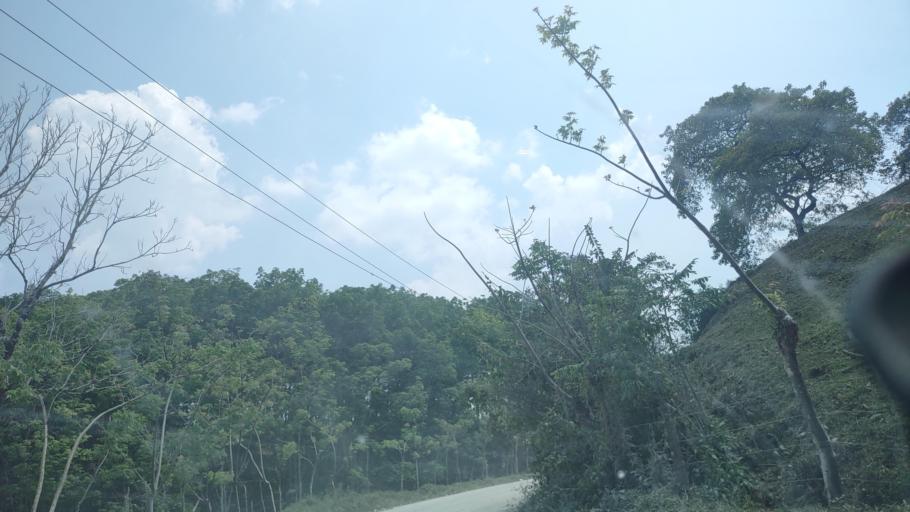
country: MX
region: Tabasco
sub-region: Huimanguillo
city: Francisco Rueda
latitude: 17.6052
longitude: -93.9055
